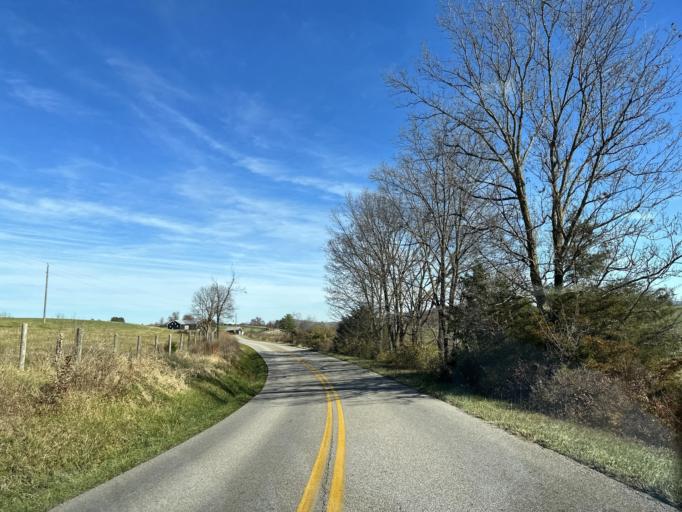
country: US
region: Virginia
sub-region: Augusta County
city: Fishersville
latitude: 38.1327
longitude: -78.9438
